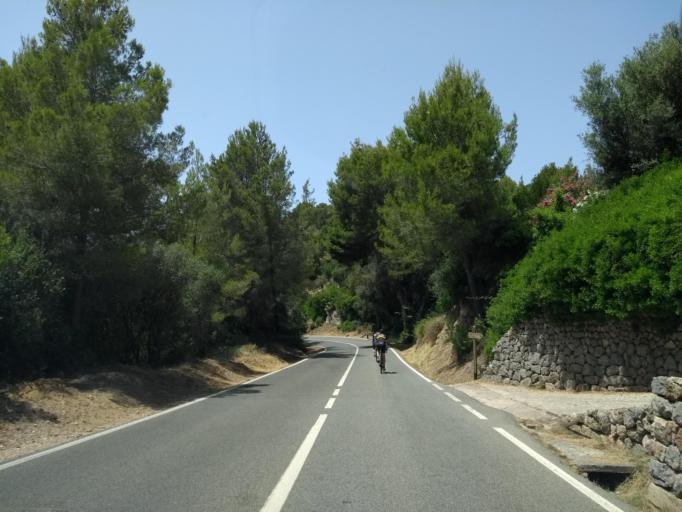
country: ES
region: Balearic Islands
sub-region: Illes Balears
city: Soller
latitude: 39.7826
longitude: 2.7147
